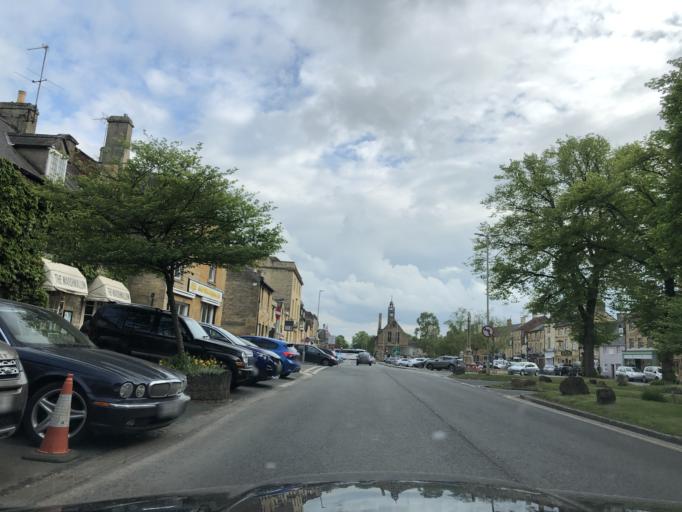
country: GB
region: England
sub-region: Gloucestershire
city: Moreton in Marsh
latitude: 51.9917
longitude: -1.7027
